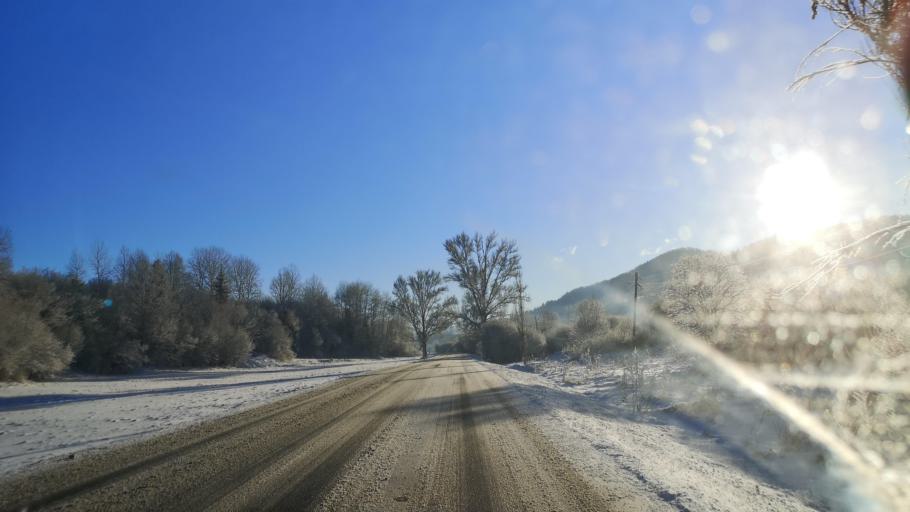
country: SK
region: Banskobystricky
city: Tisovec
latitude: 48.8547
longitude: 19.9918
